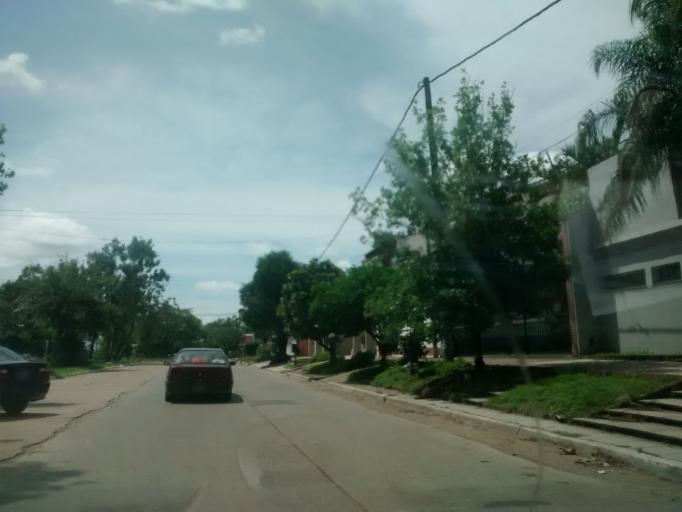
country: AR
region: Chaco
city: Resistencia
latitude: -27.4396
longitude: -58.9856
